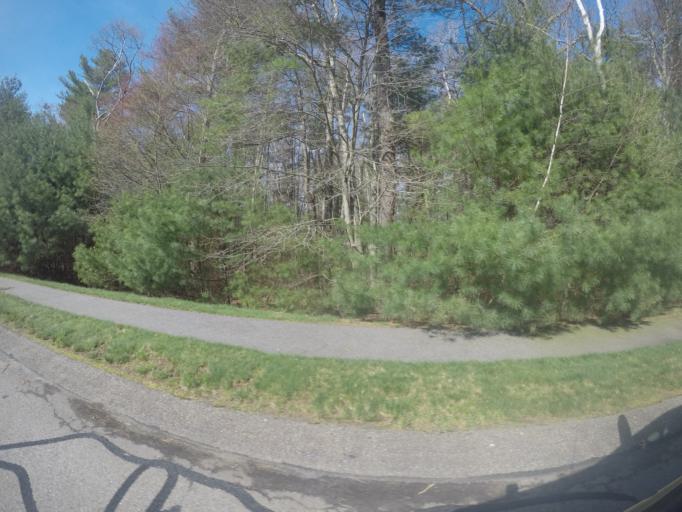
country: US
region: Massachusetts
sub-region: Bristol County
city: Easton
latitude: 42.0150
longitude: -71.1184
